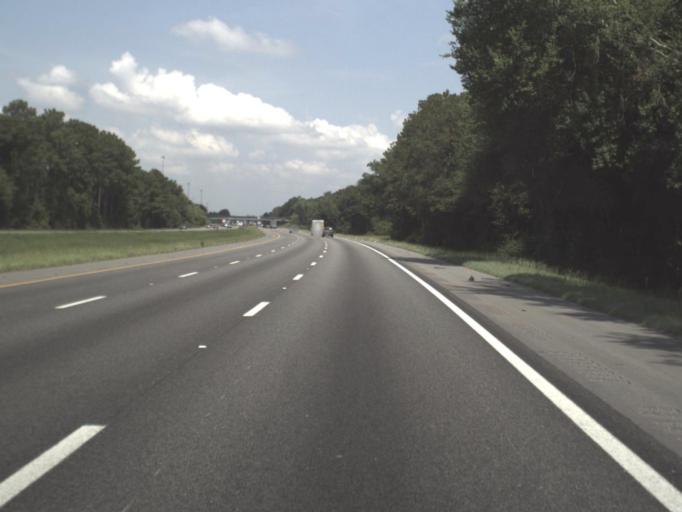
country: US
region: Georgia
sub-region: Echols County
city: Statenville
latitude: 30.6090
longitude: -83.1352
